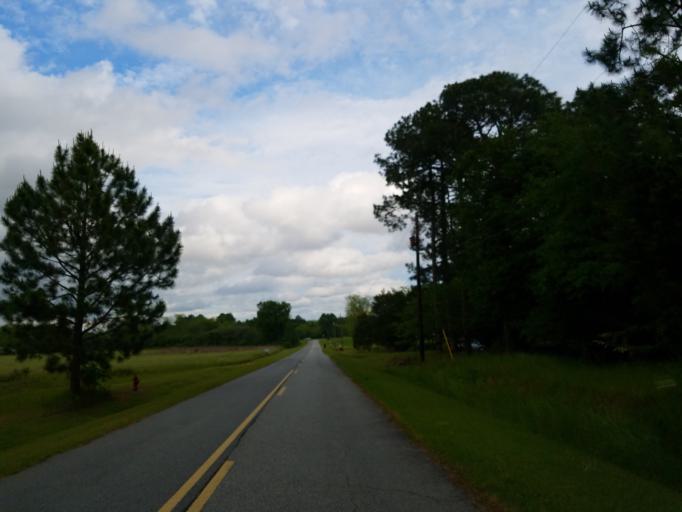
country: US
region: Georgia
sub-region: Dooly County
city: Unadilla
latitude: 32.2534
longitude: -83.7437
